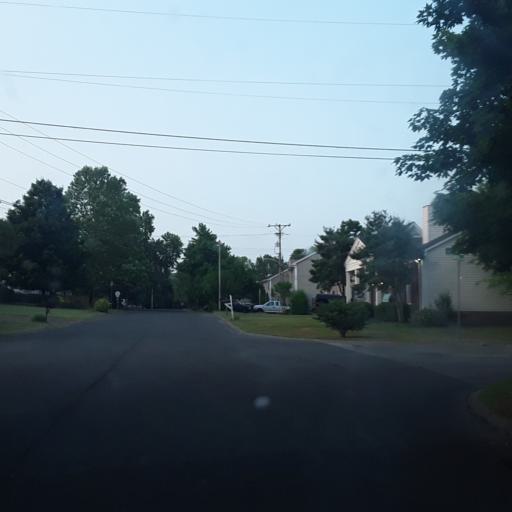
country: US
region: Tennessee
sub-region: Williamson County
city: Brentwood Estates
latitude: 36.0458
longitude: -86.7351
